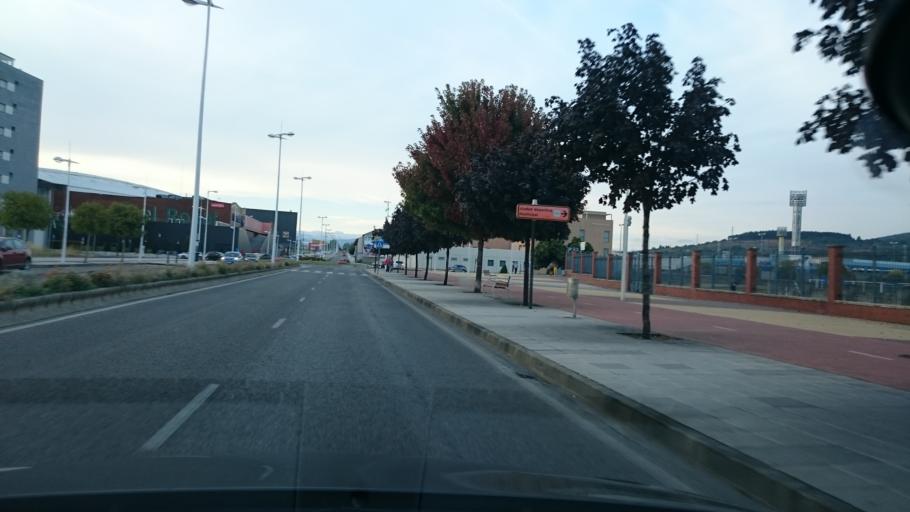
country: ES
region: Castille and Leon
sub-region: Provincia de Leon
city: Ponferrada
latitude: 42.5549
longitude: -6.6010
